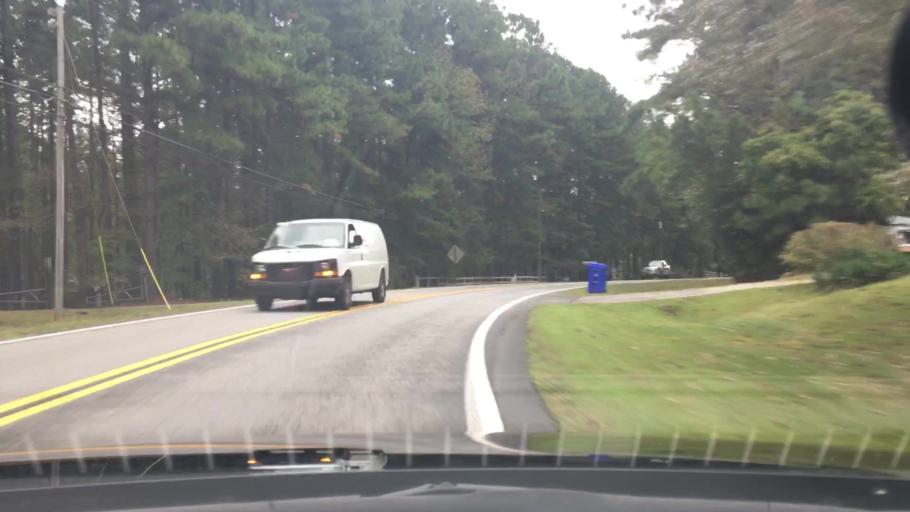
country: US
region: Georgia
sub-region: Coweta County
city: East Newnan
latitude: 33.4105
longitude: -84.7071
